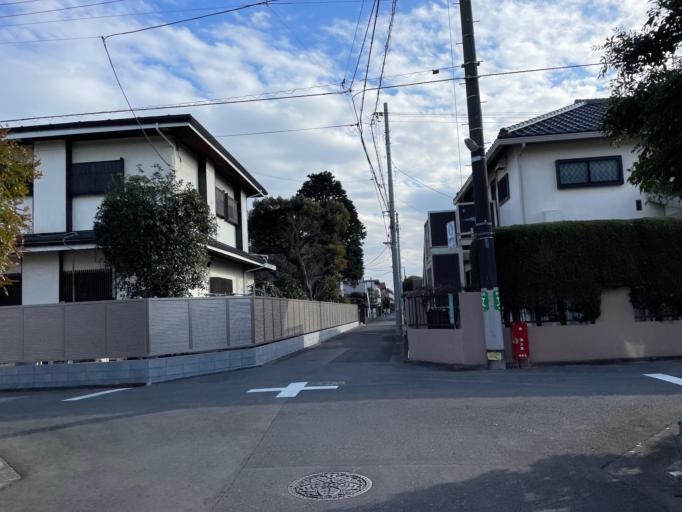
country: JP
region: Tokyo
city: Musashino
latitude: 35.7438
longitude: 139.5914
